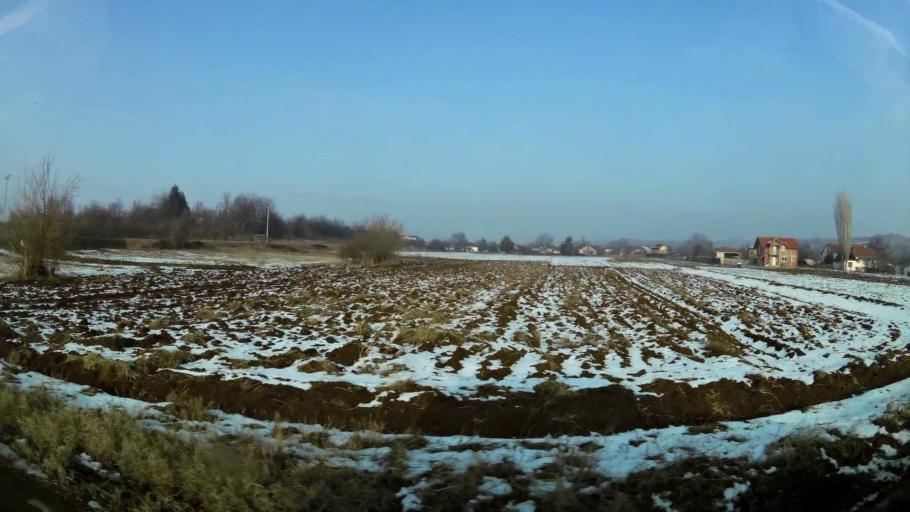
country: MK
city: Miladinovci
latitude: 41.9744
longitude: 21.6417
